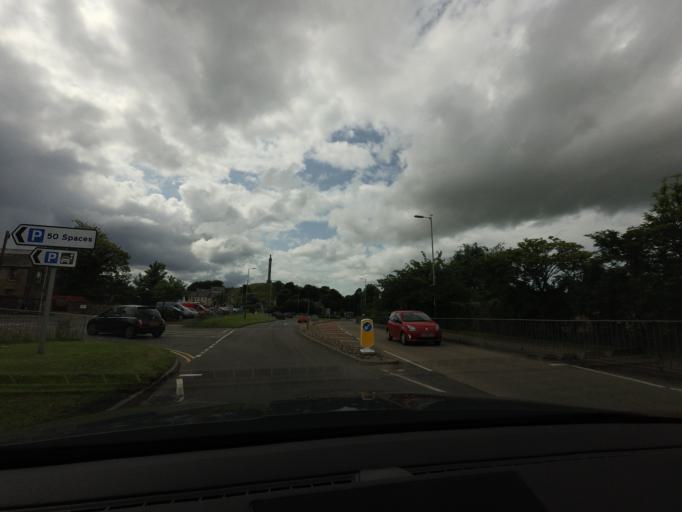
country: GB
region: Scotland
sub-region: Moray
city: Elgin
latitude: 57.6492
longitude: -3.3183
